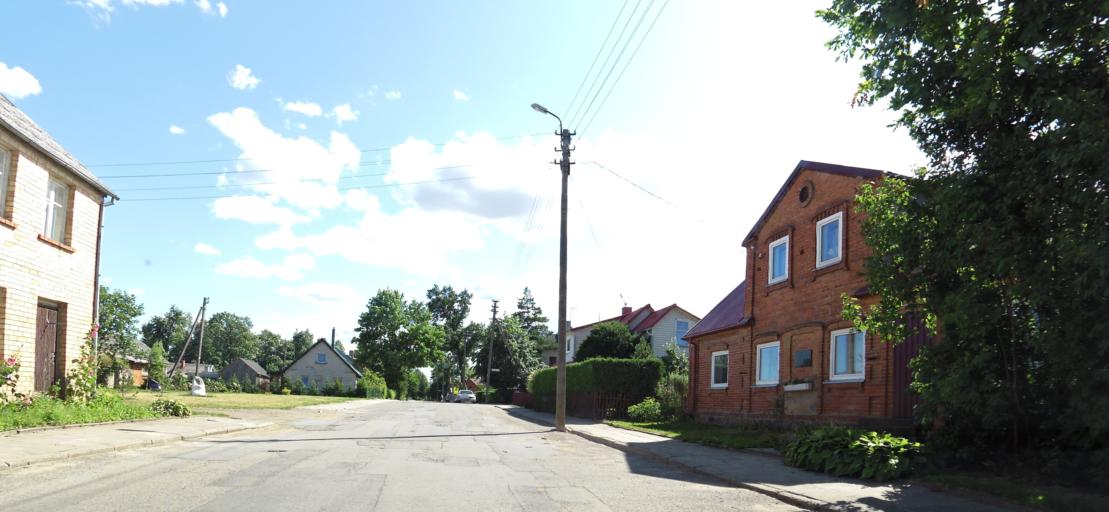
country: LT
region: Panevezys
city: Pasvalys
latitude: 56.1677
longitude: 24.2108
